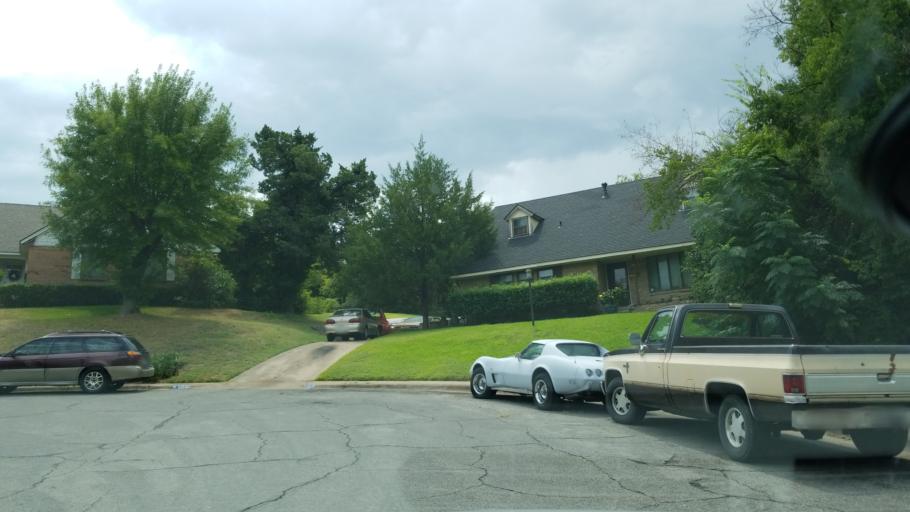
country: US
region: Texas
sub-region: Dallas County
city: Duncanville
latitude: 32.6672
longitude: -96.8419
